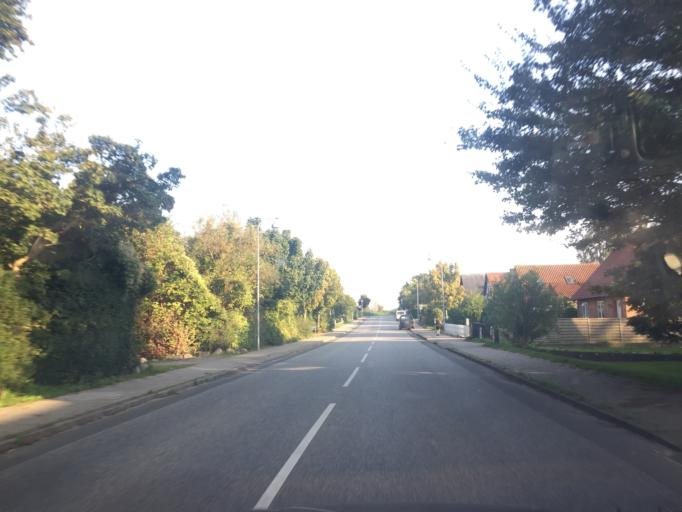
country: DK
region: Zealand
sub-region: Kalundborg Kommune
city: Svebolle
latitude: 55.6179
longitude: 11.2187
